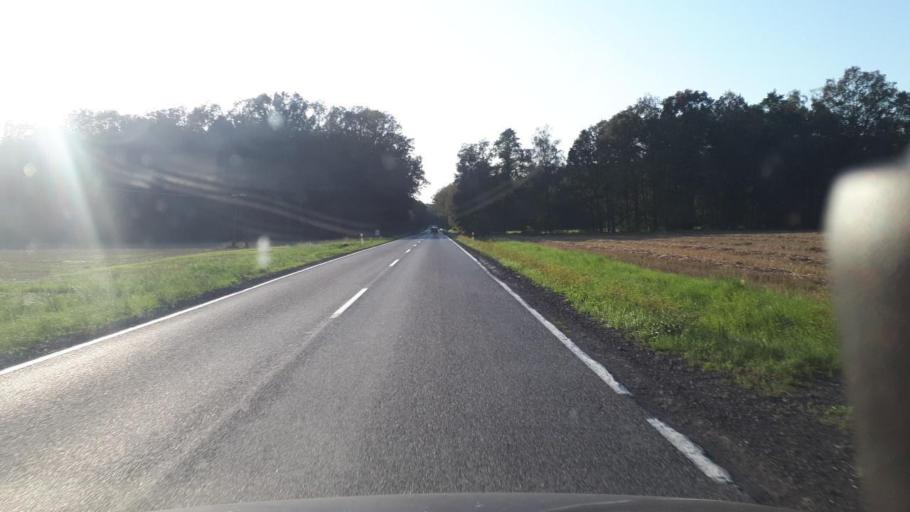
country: PL
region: Opole Voivodeship
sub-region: Powiat oleski
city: Olesno
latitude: 50.8469
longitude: 18.4814
